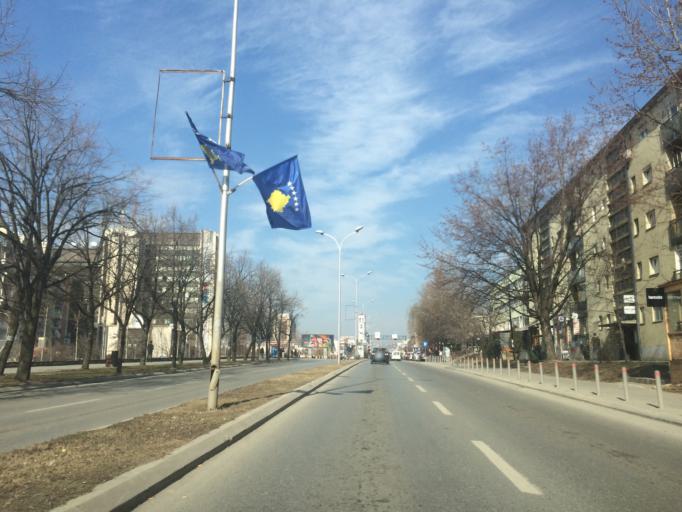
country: XK
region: Pristina
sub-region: Komuna e Prishtines
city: Pristina
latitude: 42.6496
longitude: 21.1581
